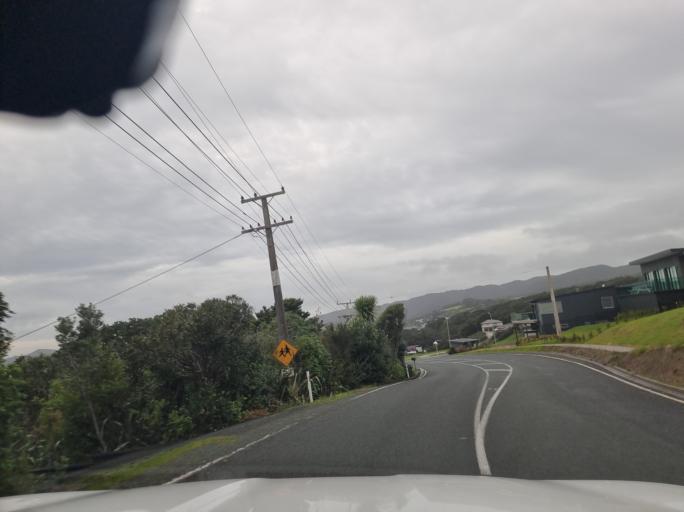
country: NZ
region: Northland
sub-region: Whangarei
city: Ruakaka
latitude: -36.0379
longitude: 174.5233
